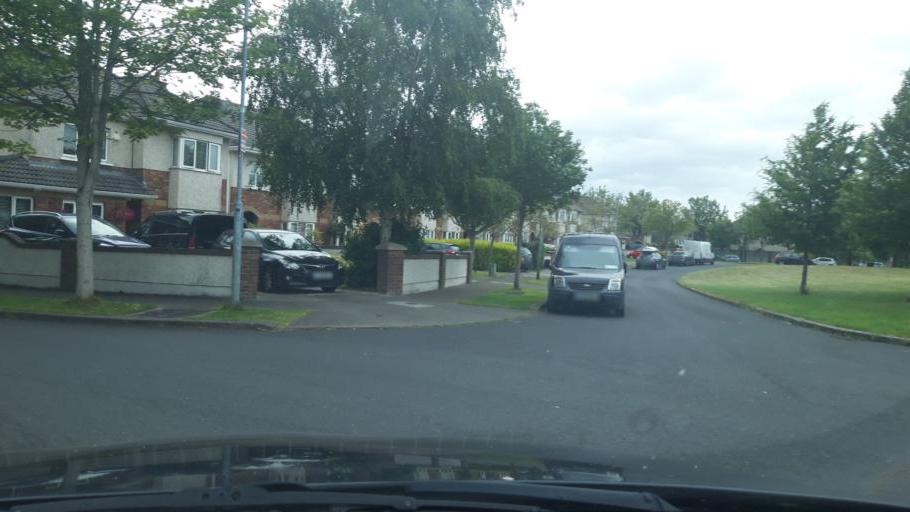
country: IE
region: Leinster
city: Hartstown
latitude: 53.4020
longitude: -6.4206
